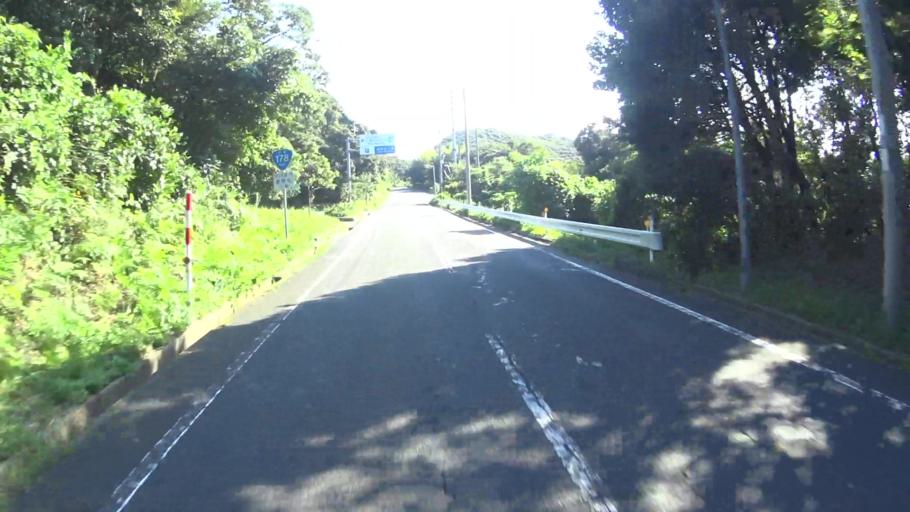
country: JP
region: Kyoto
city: Miyazu
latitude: 35.7071
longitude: 135.0693
